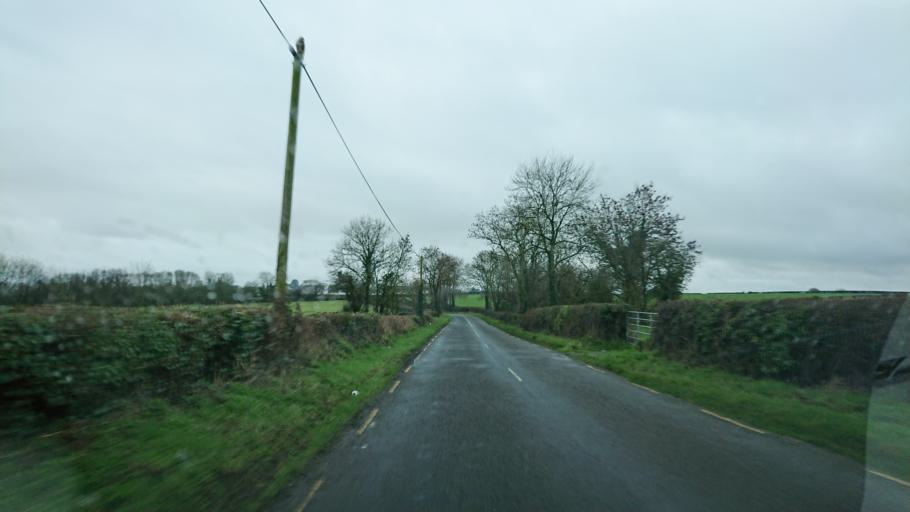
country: IE
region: Leinster
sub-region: Kilkenny
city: Callan
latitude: 52.5320
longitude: -7.2952
